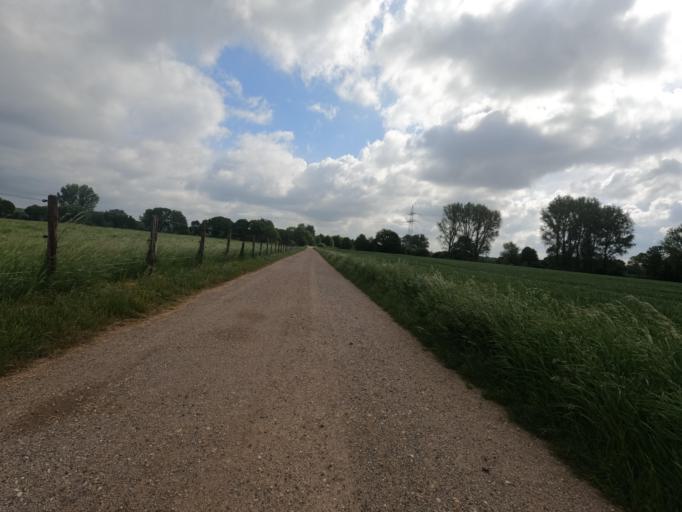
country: DE
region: North Rhine-Westphalia
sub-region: Regierungsbezirk Koln
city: Wassenberg
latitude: 51.0700
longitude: 6.1480
